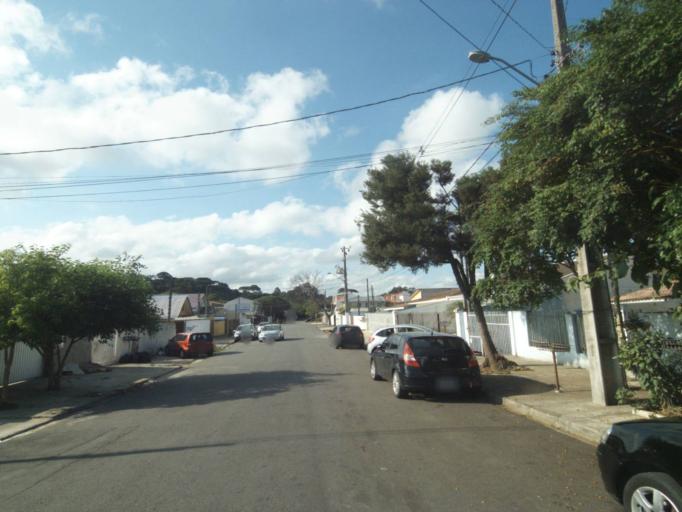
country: BR
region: Parana
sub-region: Curitiba
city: Curitiba
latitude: -25.3899
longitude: -49.3026
